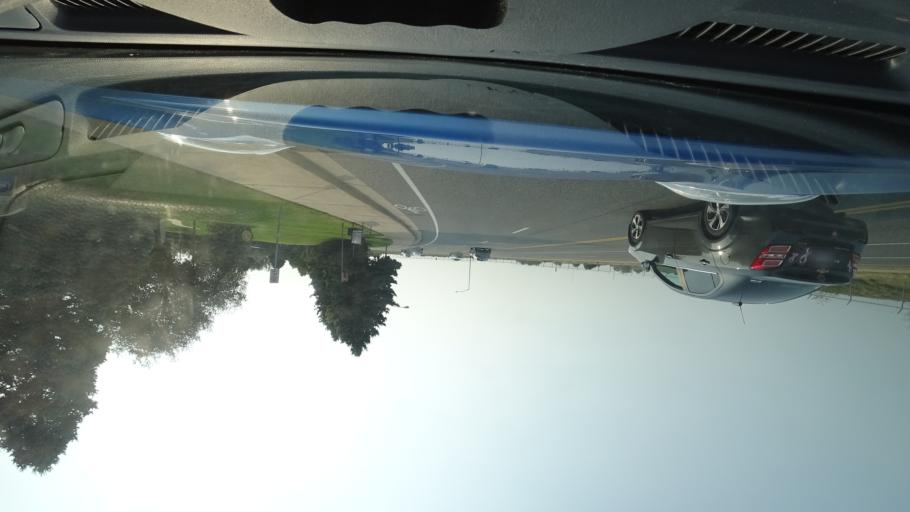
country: US
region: Colorado
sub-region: Adams County
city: Aurora
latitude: 39.6683
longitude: -104.8148
